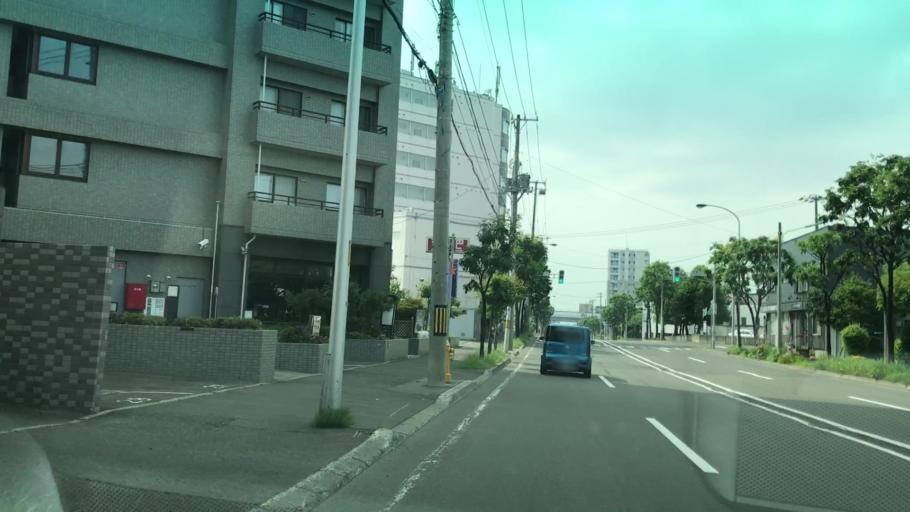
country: JP
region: Hokkaido
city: Sapporo
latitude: 43.0907
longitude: 141.2884
